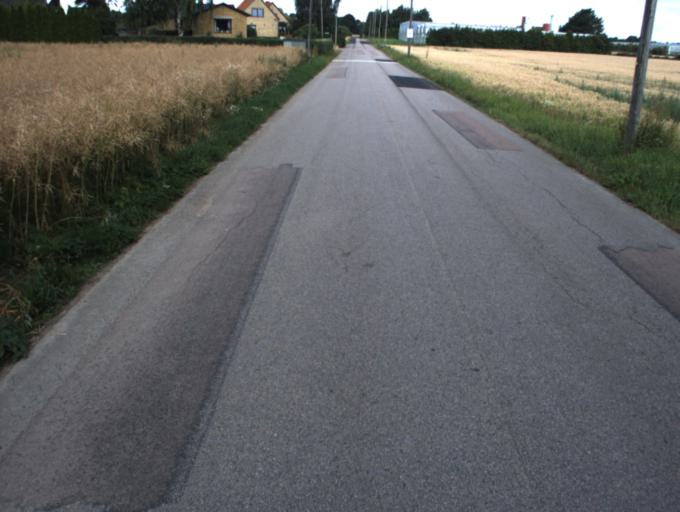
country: SE
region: Skane
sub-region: Helsingborg
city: Gantofta
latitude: 56.0077
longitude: 12.7880
